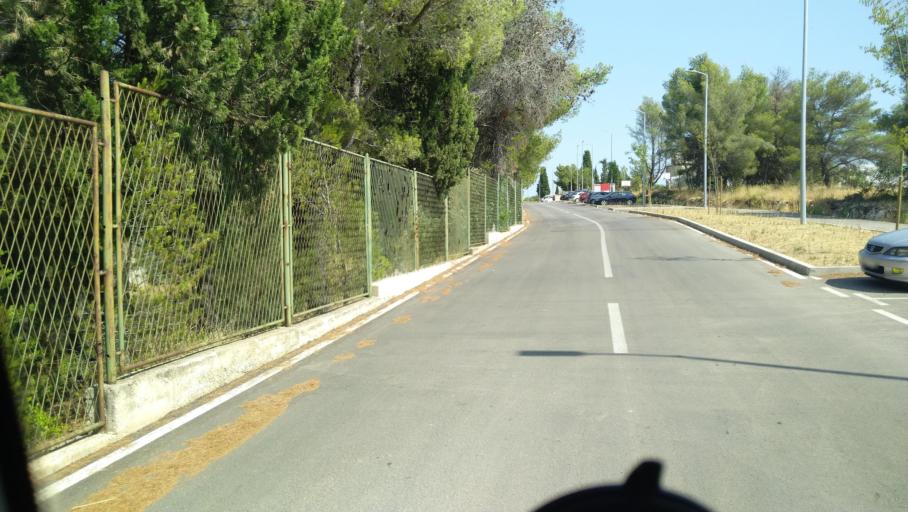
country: HR
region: Sibensko-Kniniska
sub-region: Grad Sibenik
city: Sibenik
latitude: 43.7174
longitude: 15.9069
